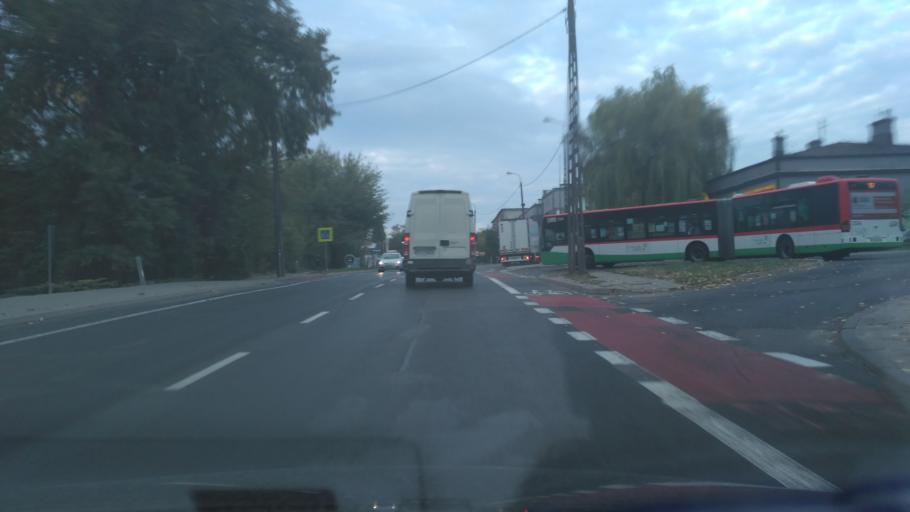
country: PL
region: Lublin Voivodeship
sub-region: Powiat lubelski
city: Jakubowice Murowane
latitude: 51.2540
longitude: 22.6030
